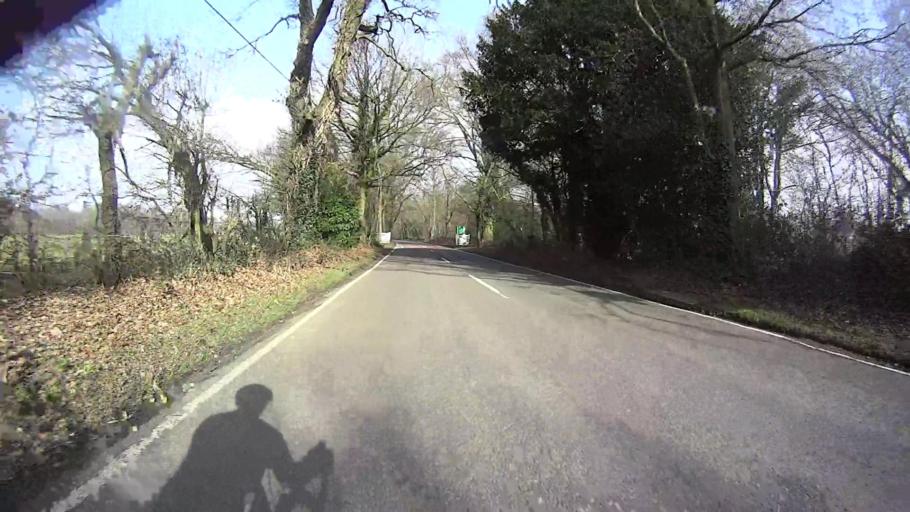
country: GB
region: England
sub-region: Surrey
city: Headley
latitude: 51.2567
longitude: -0.2724
